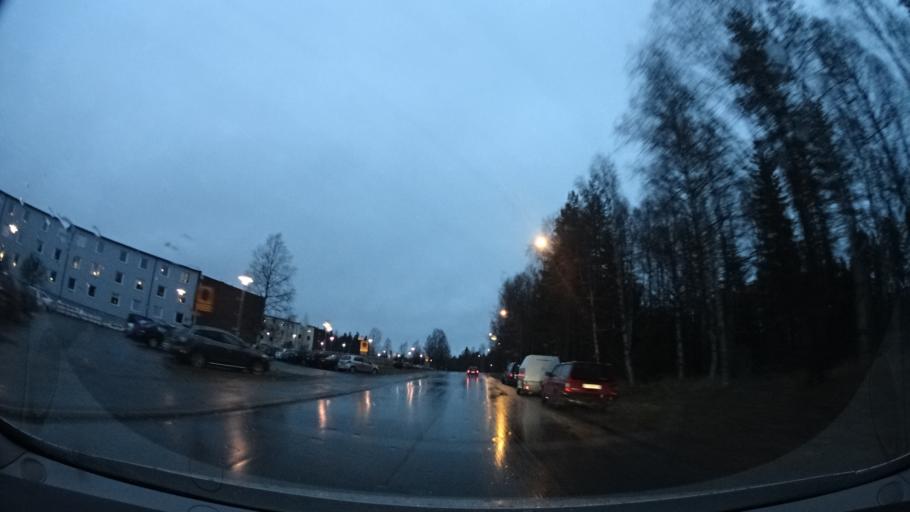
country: SE
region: Vaesterbotten
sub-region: Skelleftea Kommun
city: Skelleftea
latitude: 64.7546
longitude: 21.0143
